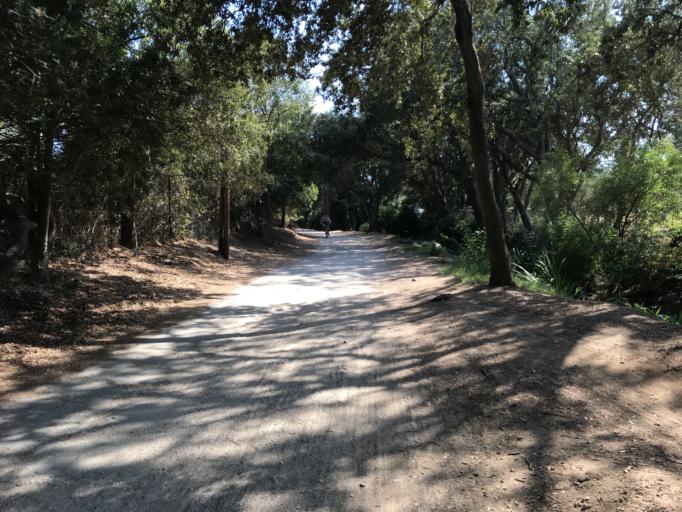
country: FR
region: Provence-Alpes-Cote d'Azur
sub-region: Departement du Var
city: Hyeres
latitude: 42.9943
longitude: 6.2029
